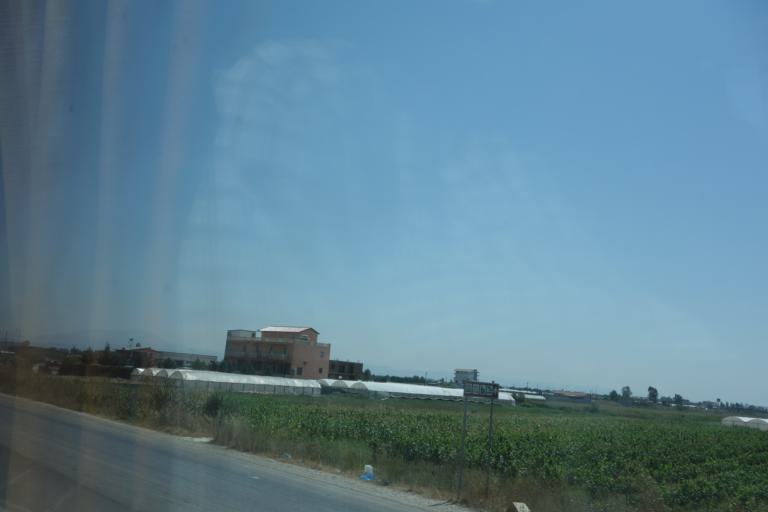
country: AL
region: Fier
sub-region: Rrethi i Lushnjes
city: Karbunara e Vogel
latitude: 40.9217
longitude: 19.7006
